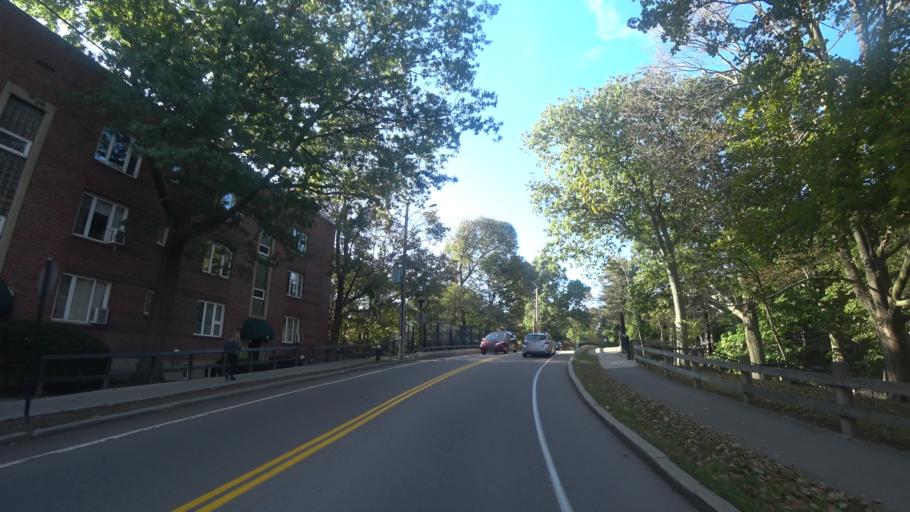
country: US
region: Massachusetts
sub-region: Norfolk County
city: Brookline
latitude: 42.3365
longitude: -71.1415
